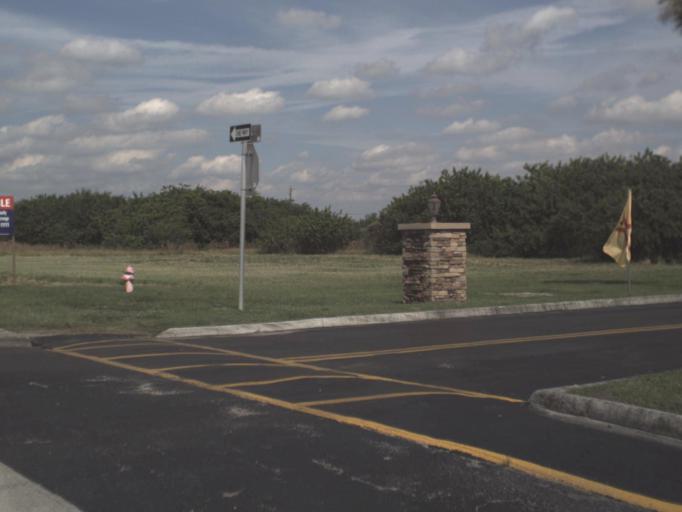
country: US
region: Florida
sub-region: Okeechobee County
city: Okeechobee
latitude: 27.2049
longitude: -80.8297
